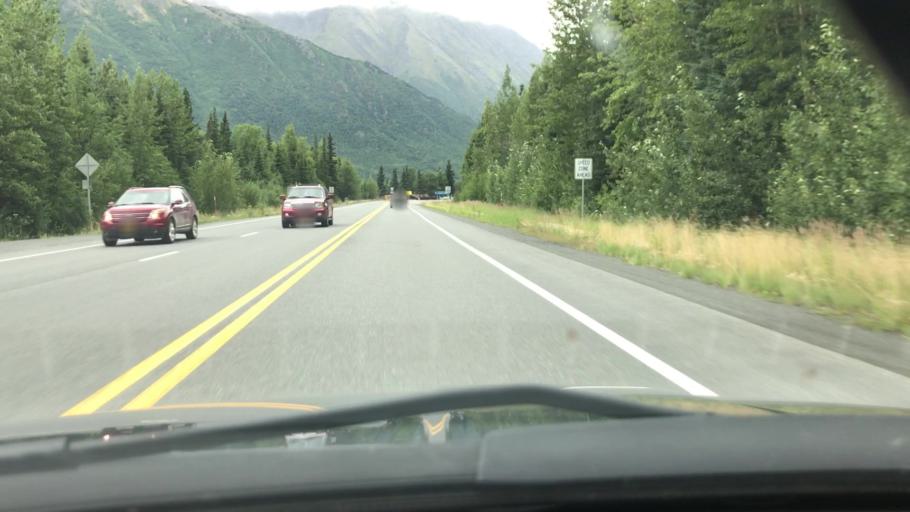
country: US
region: Alaska
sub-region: Kenai Peninsula Borough
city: Bear Creek
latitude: 60.4869
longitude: -149.7268
